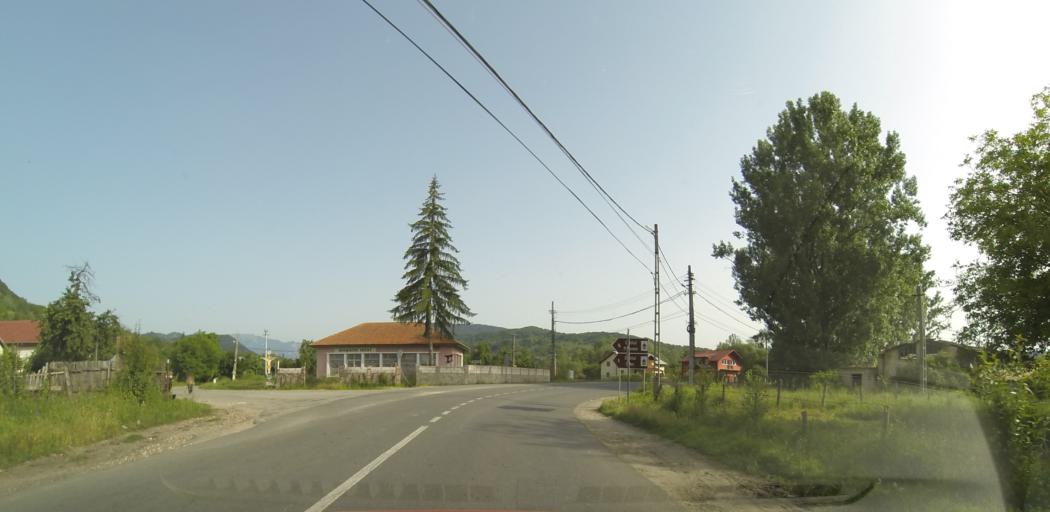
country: RO
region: Valcea
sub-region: Comuna Pausesti-Maglasi
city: Pausesti-Maglasi
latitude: 45.1570
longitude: 24.2476
